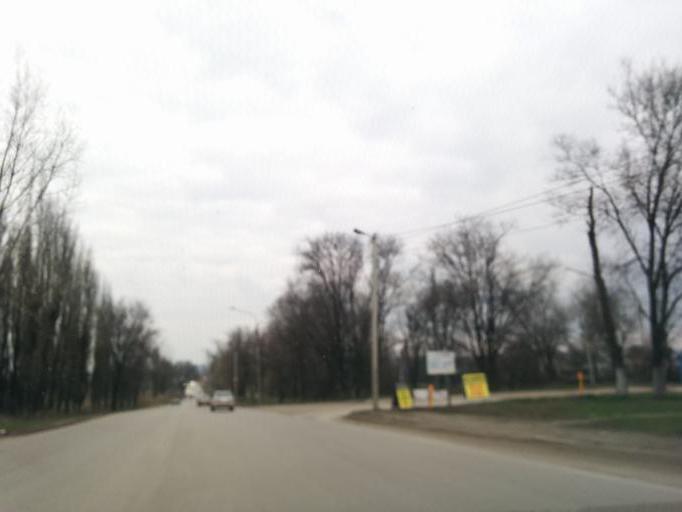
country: RU
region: Rostov
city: Novocherkassk
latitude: 47.4641
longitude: 40.0997
